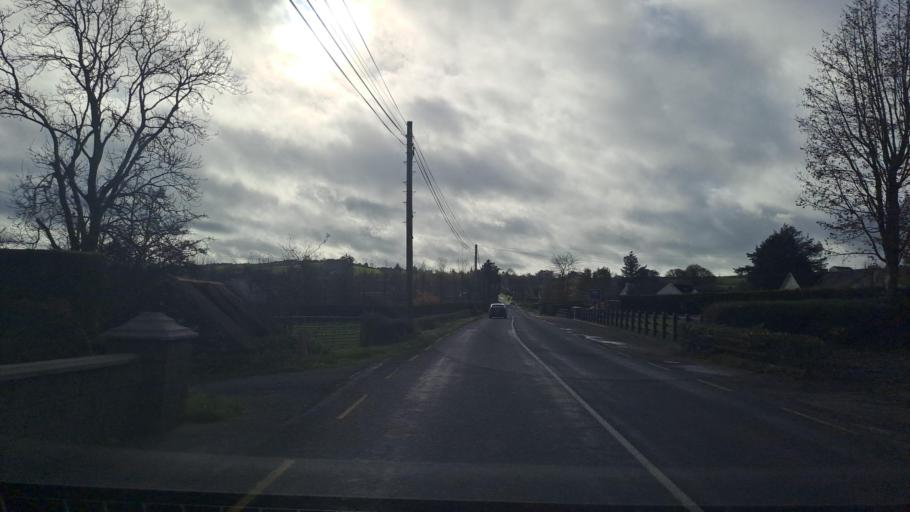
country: IE
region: Ulster
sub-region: County Monaghan
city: Monaghan
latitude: 54.1993
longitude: -6.9883
